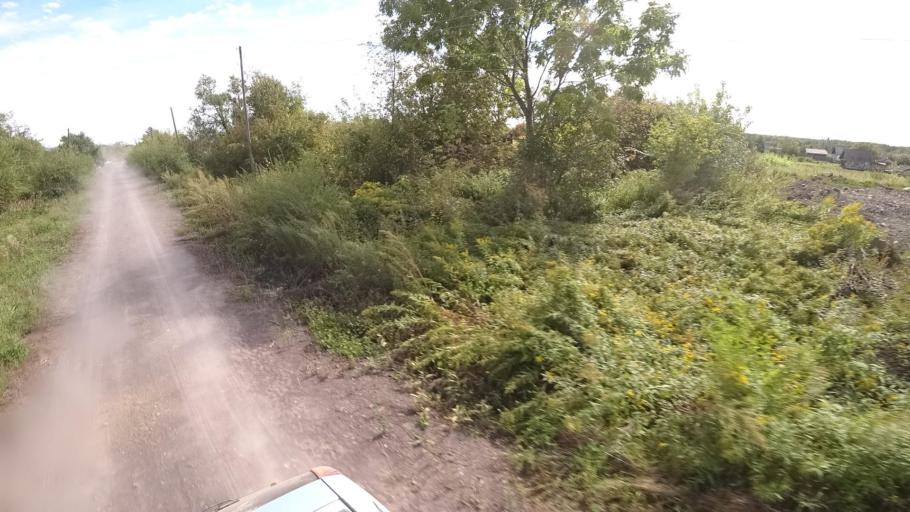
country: RU
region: Primorskiy
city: Yakovlevka
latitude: 44.4366
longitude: 133.5625
